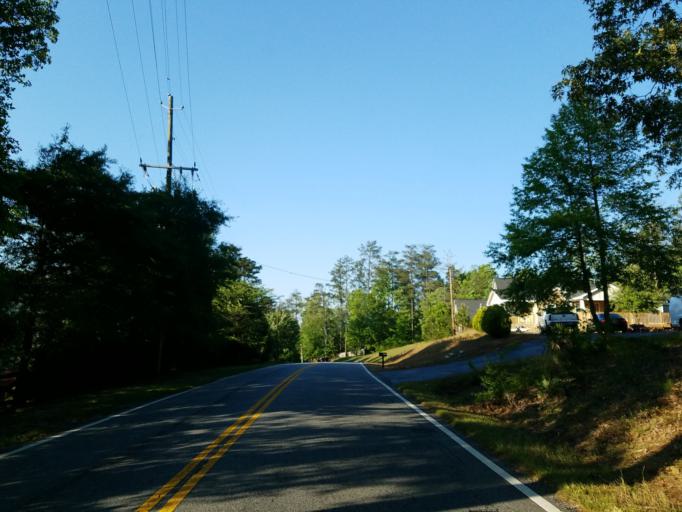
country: US
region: Georgia
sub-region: Cobb County
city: Mableton
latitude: 33.8332
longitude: -84.5376
